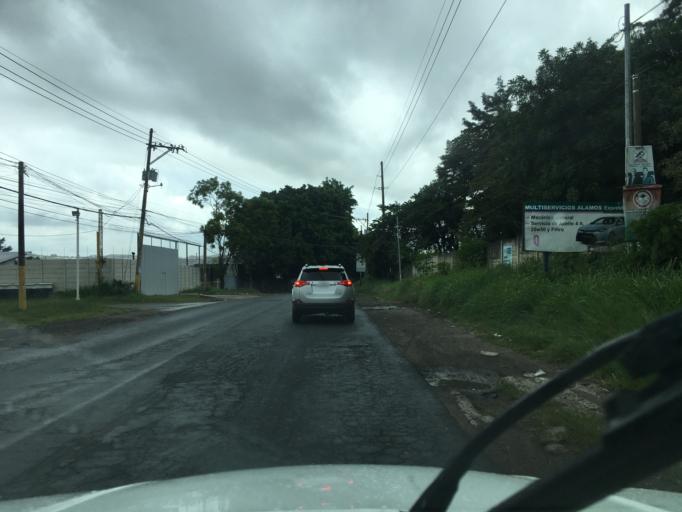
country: GT
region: Guatemala
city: Petapa
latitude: 14.5198
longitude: -90.5346
